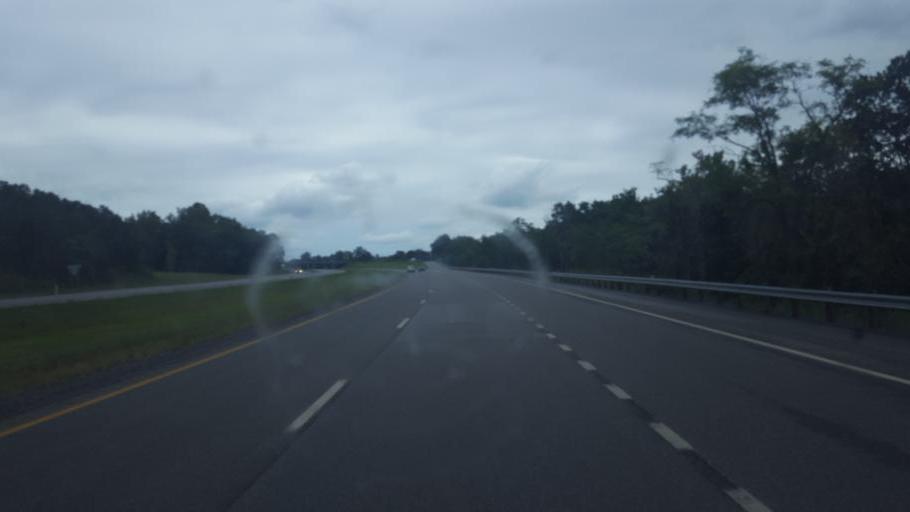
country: US
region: Ohio
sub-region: Lake County
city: Painesville
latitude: 41.6892
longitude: -81.2549
